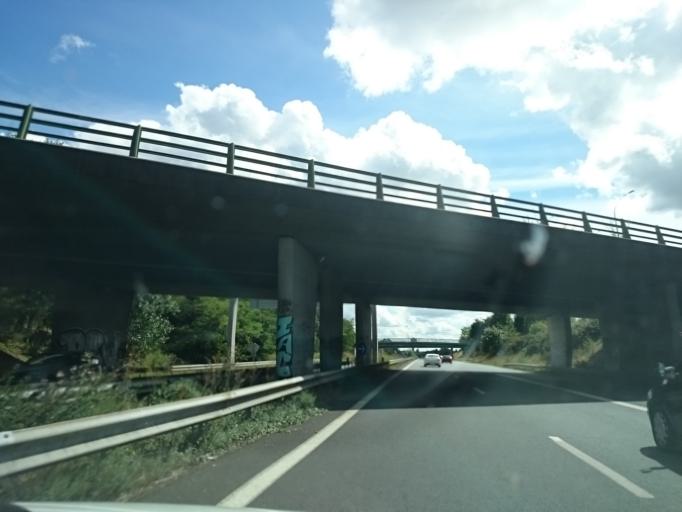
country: FR
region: Pays de la Loire
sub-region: Departement de la Loire-Atlantique
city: Sainte-Luce-sur-Loire
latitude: 47.2700
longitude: -1.4799
